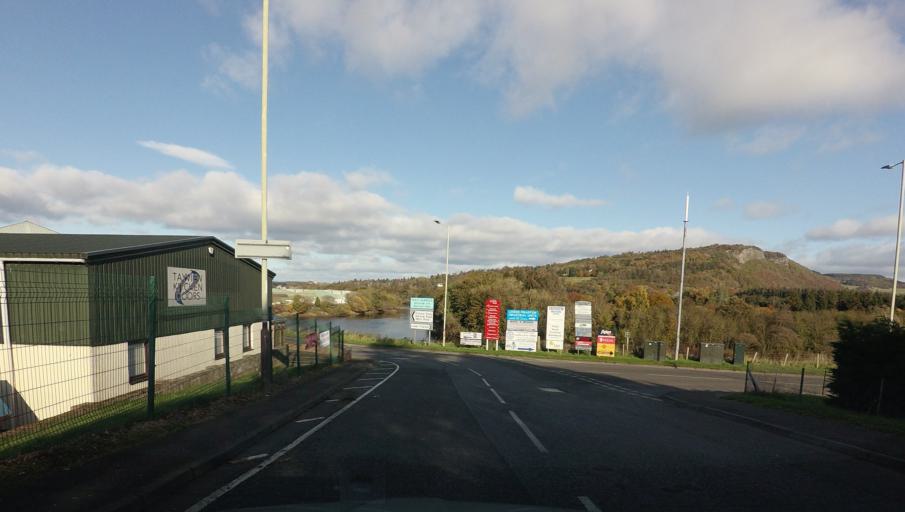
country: GB
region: Scotland
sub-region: Perth and Kinross
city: Perth
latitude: 56.3779
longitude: -3.4278
